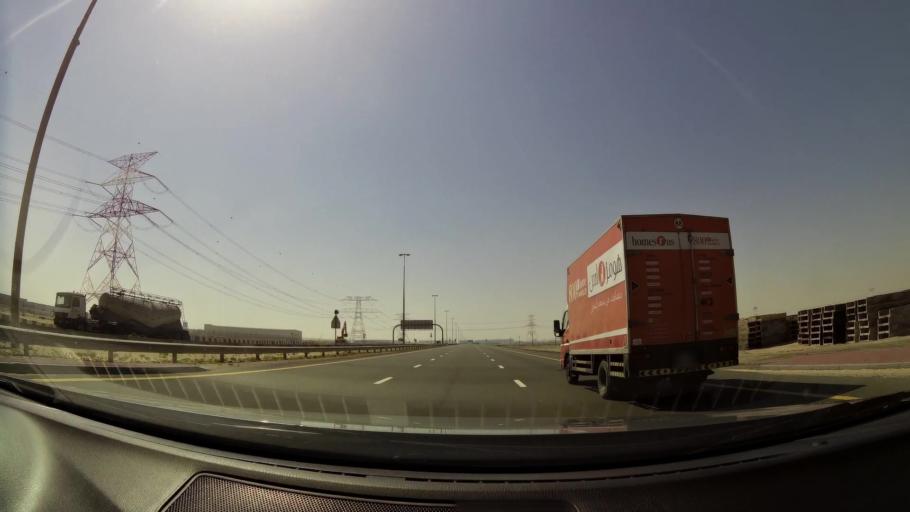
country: AE
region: Dubai
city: Dubai
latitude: 24.9264
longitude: 55.0929
